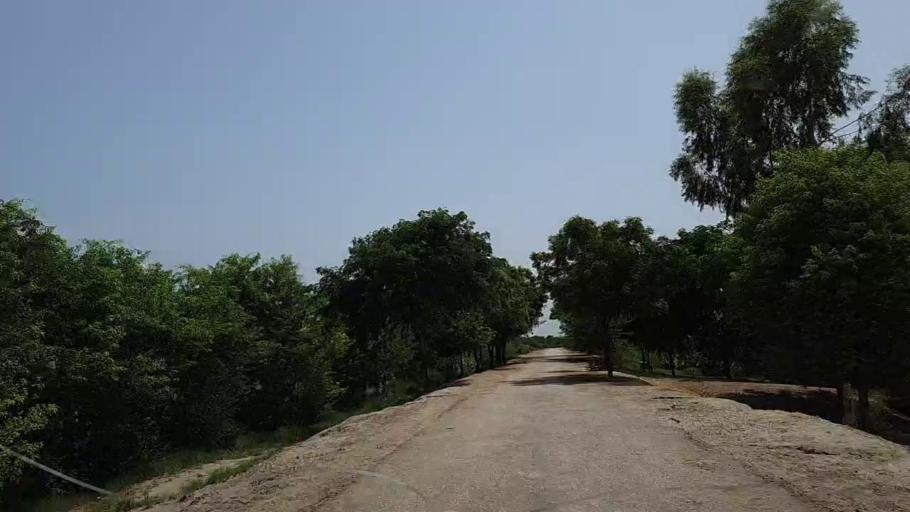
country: PK
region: Sindh
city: Kandiaro
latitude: 27.0485
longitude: 68.1335
